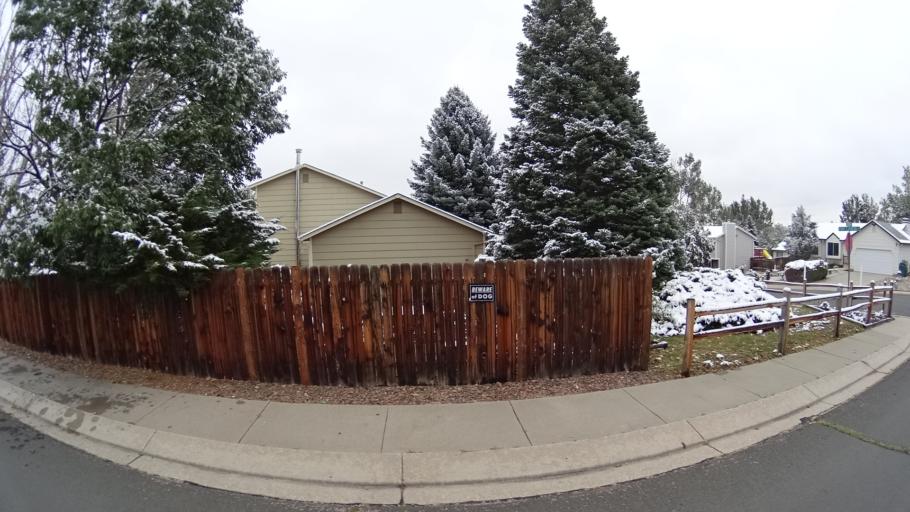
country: US
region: Colorado
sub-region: El Paso County
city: Cimarron Hills
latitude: 38.9267
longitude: -104.7688
